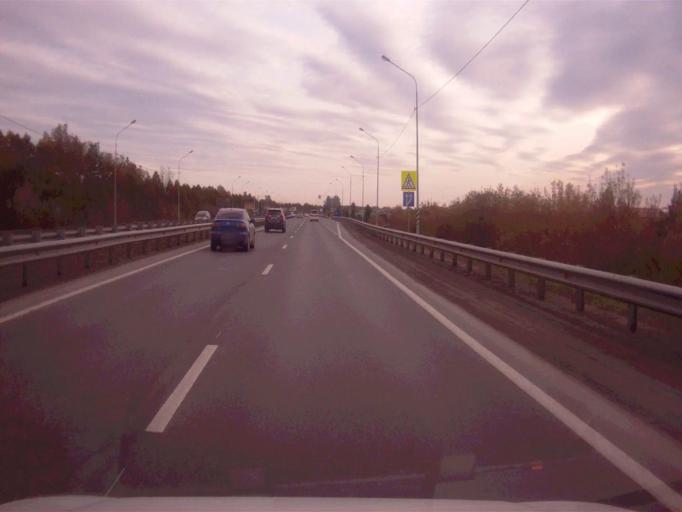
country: RU
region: Chelyabinsk
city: Novosineglazovskiy
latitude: 55.0331
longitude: 61.4441
